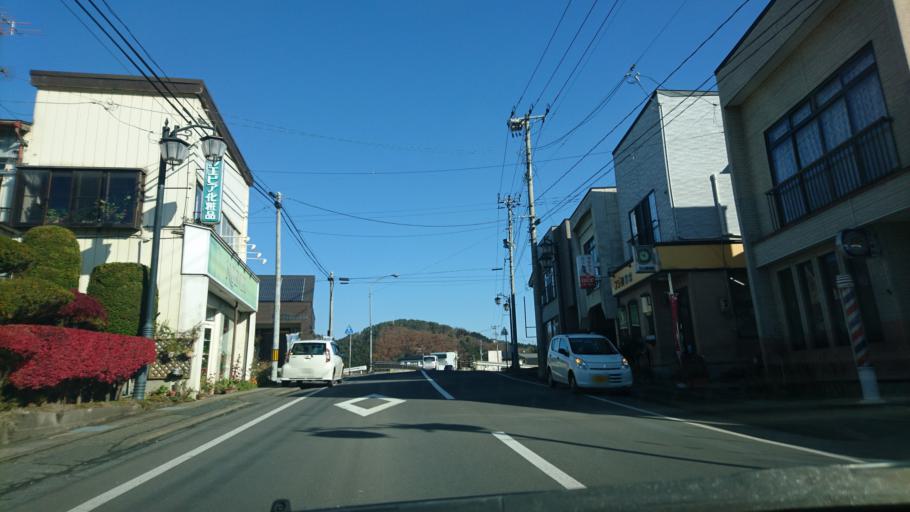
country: JP
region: Iwate
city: Ichinoseki
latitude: 38.9932
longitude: 141.2525
